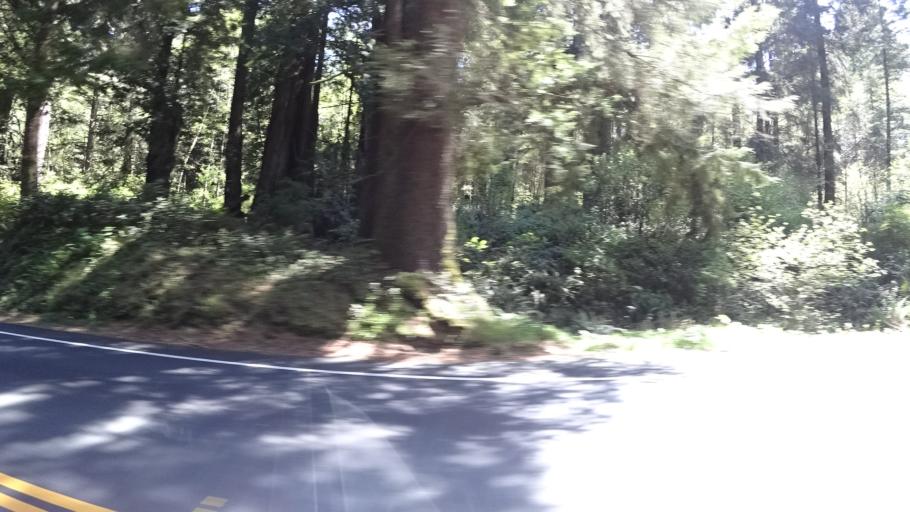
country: US
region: California
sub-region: Humboldt County
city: Westhaven-Moonstone
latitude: 41.1701
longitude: -124.1019
